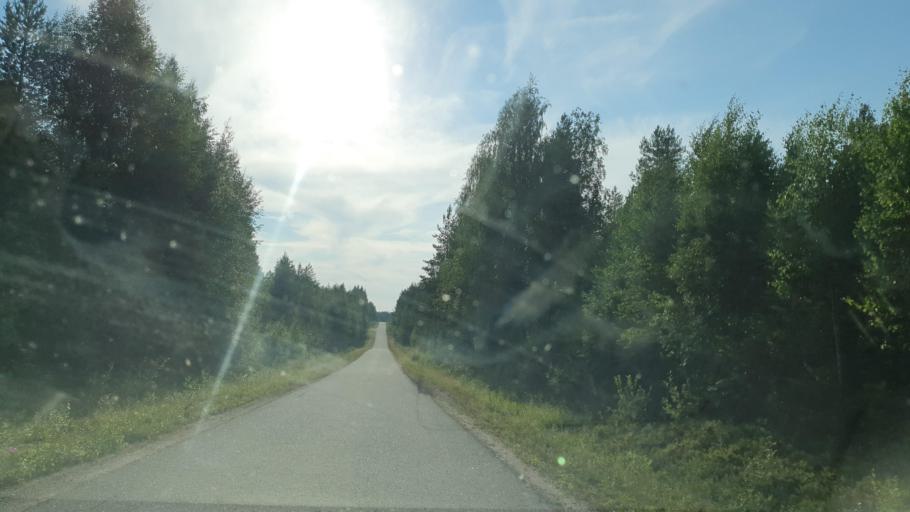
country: FI
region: Kainuu
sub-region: Kehys-Kainuu
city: Kuhmo
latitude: 64.2804
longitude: 29.4168
